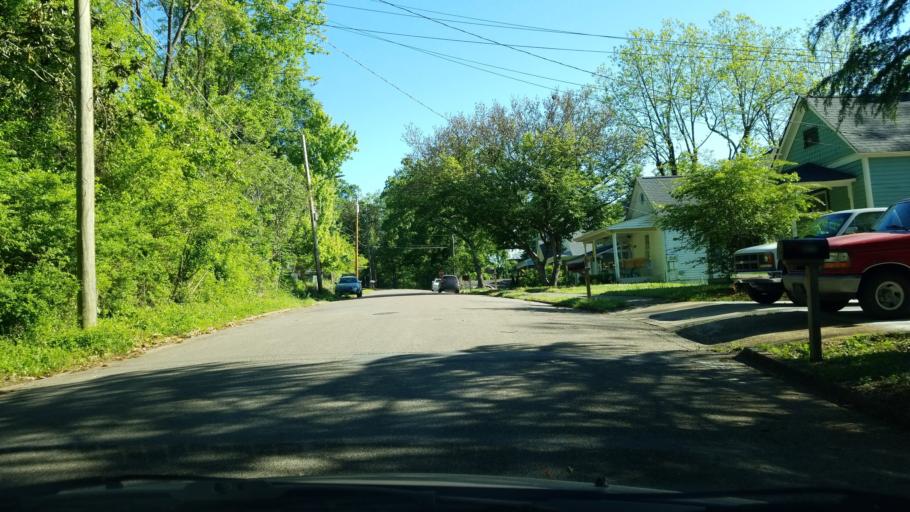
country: US
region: Tennessee
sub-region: Hamilton County
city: Lookout Mountain
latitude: 34.9888
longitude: -85.3328
